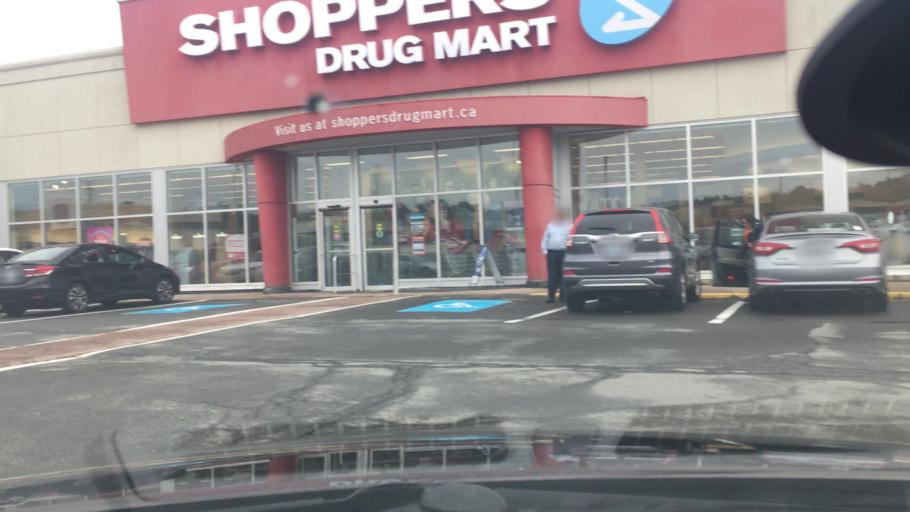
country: CA
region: Nova Scotia
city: Dartmouth
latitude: 44.7730
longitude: -63.6938
